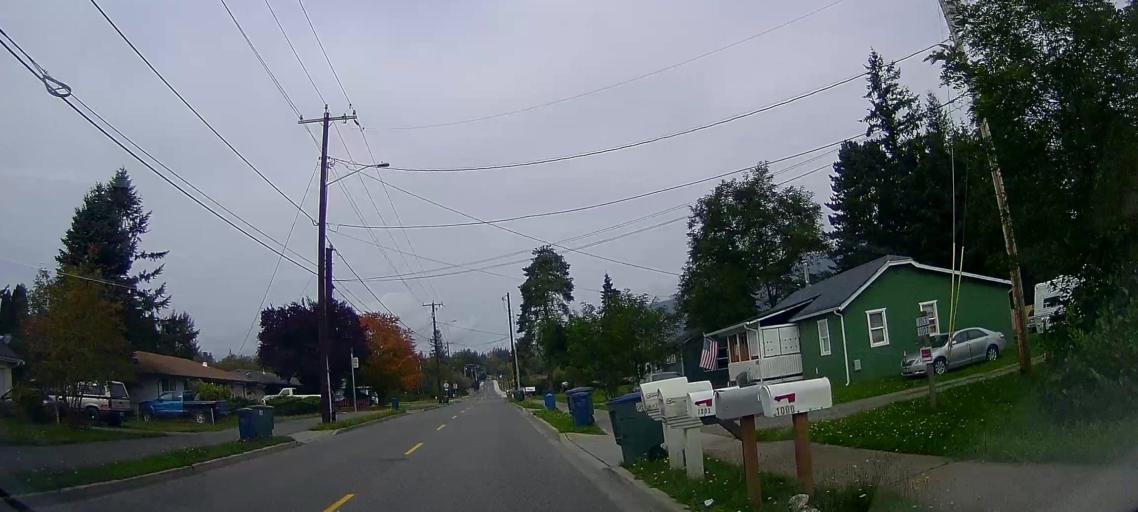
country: US
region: Washington
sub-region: Skagit County
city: Sedro-Woolley
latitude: 48.5207
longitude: -122.2105
